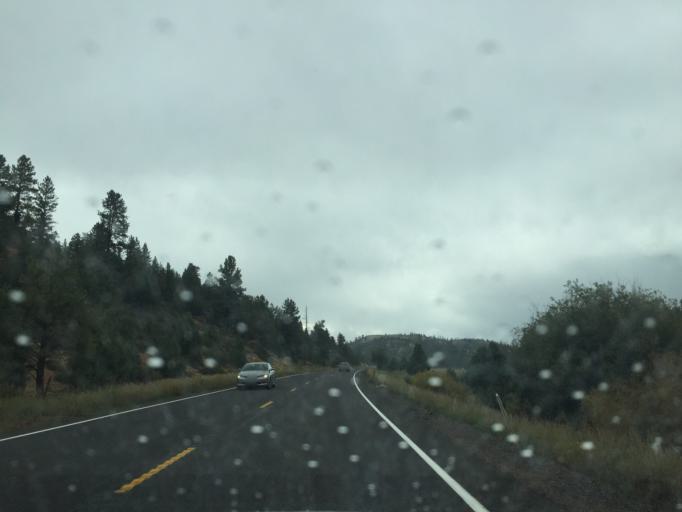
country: US
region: Utah
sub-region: Kane County
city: Kanab
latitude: 37.4323
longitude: -112.5387
